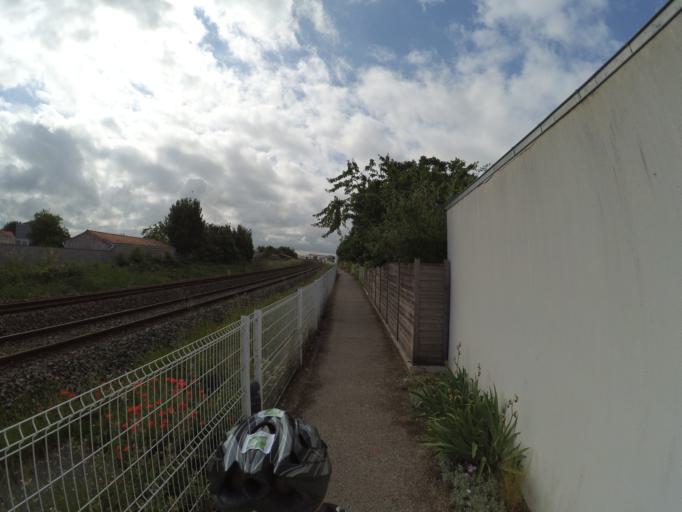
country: FR
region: Poitou-Charentes
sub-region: Departement de la Charente-Maritime
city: Angoulins
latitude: 46.1032
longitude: -1.1134
